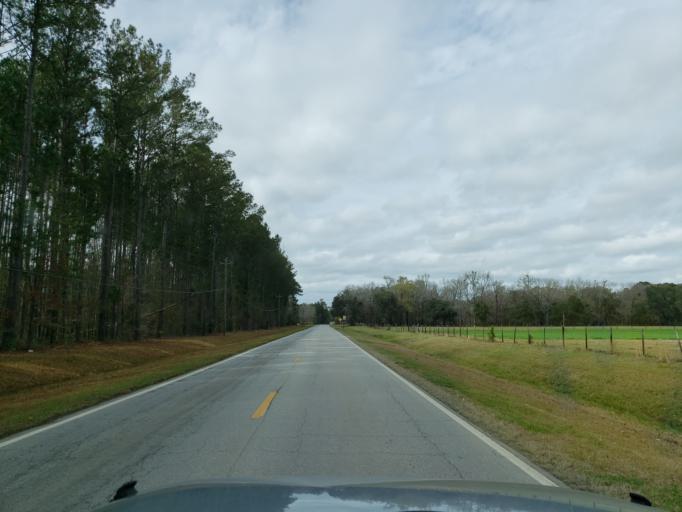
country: US
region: Georgia
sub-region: Chatham County
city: Georgetown
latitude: 32.0401
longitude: -81.2768
